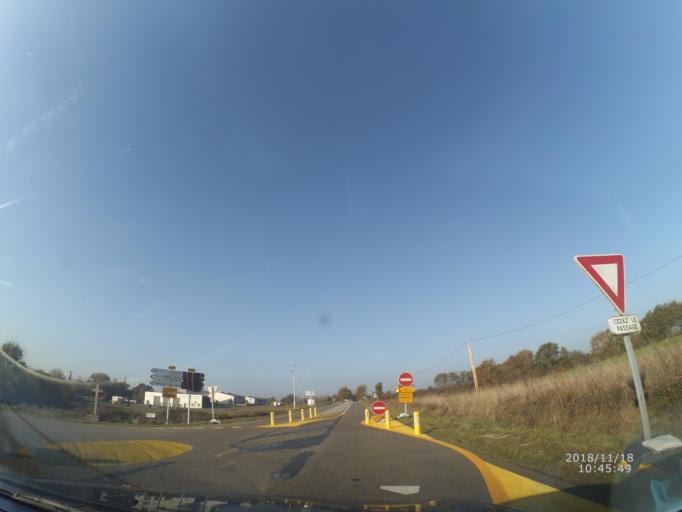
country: FR
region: Pays de la Loire
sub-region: Departement de la Loire-Atlantique
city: Vue
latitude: 47.2005
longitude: -1.9018
